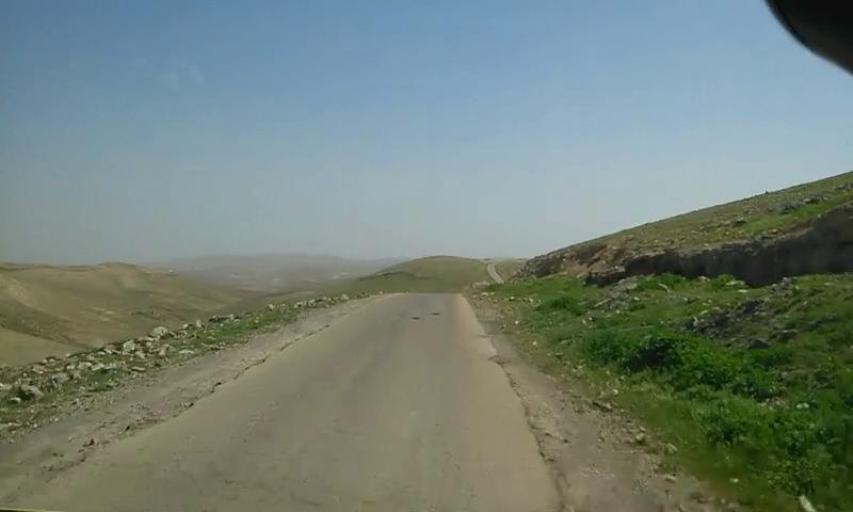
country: PS
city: `Arab ar Rashaydah
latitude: 31.5426
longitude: 35.2620
